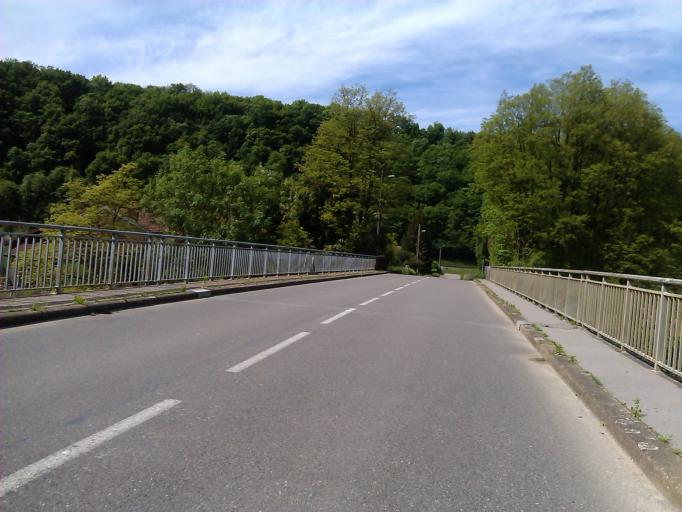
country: FR
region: Franche-Comte
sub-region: Departement du Doubs
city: Boussieres
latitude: 47.1611
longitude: 5.8866
